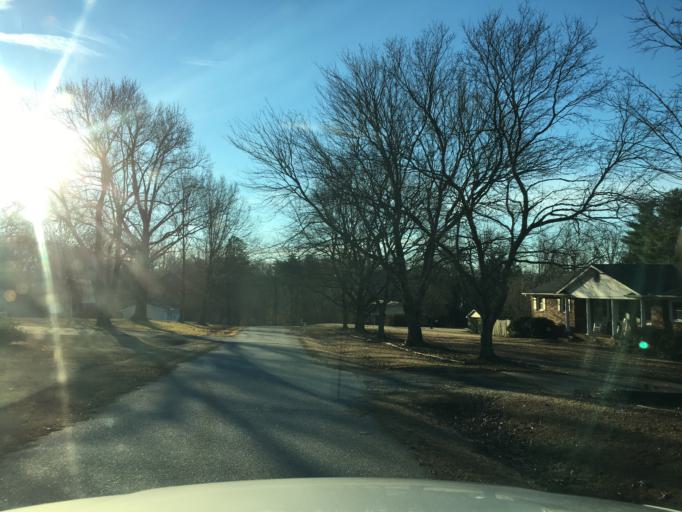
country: US
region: South Carolina
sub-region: Spartanburg County
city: Lyman
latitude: 34.9237
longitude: -82.1248
